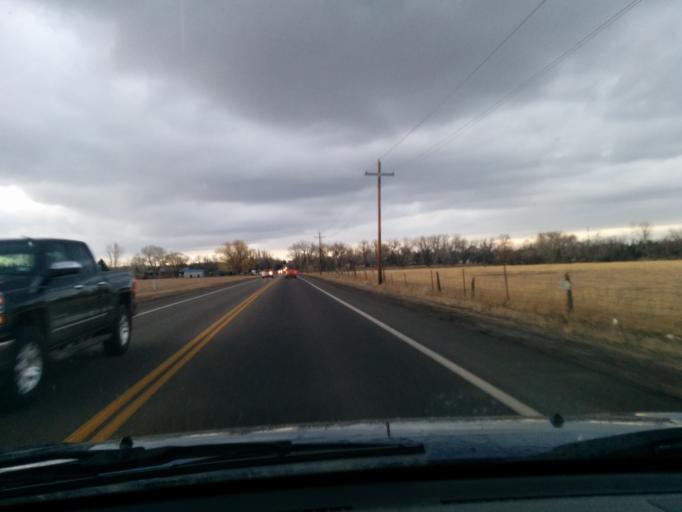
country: US
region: Colorado
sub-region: Larimer County
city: Fort Collins
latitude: 40.5997
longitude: -105.0577
